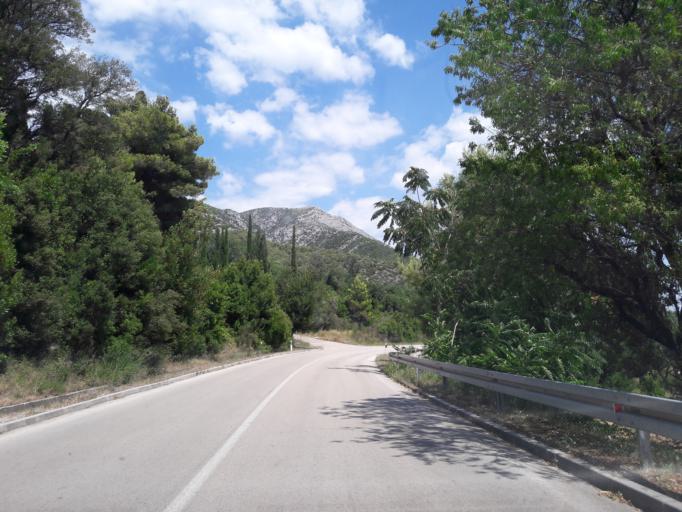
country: HR
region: Dubrovacko-Neretvanska
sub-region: Grad Korcula
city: Zrnovo
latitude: 42.9847
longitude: 17.0996
